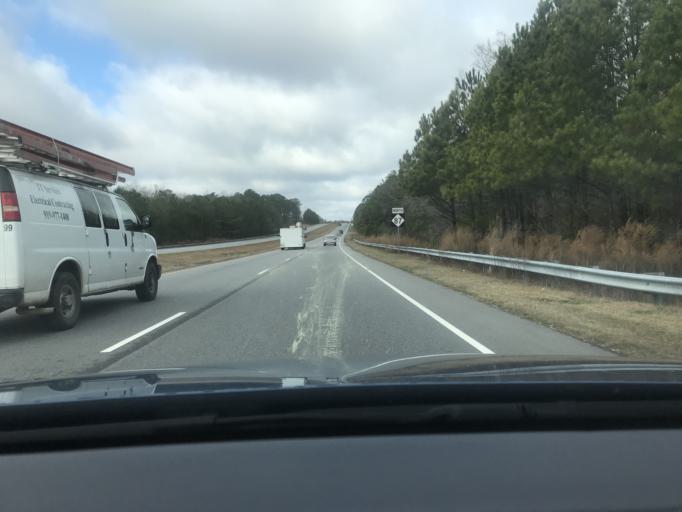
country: US
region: North Carolina
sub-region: Cumberland County
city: Spring Lake
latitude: 35.2712
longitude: -79.0624
